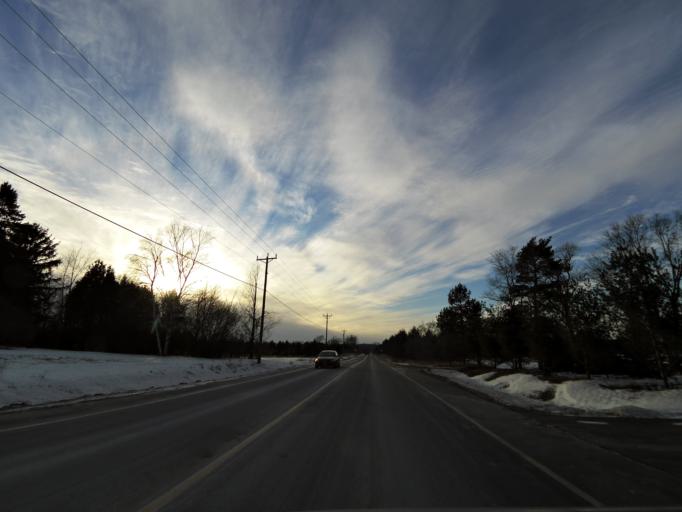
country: US
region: Minnesota
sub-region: Washington County
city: Afton
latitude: 44.8910
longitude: -92.8265
